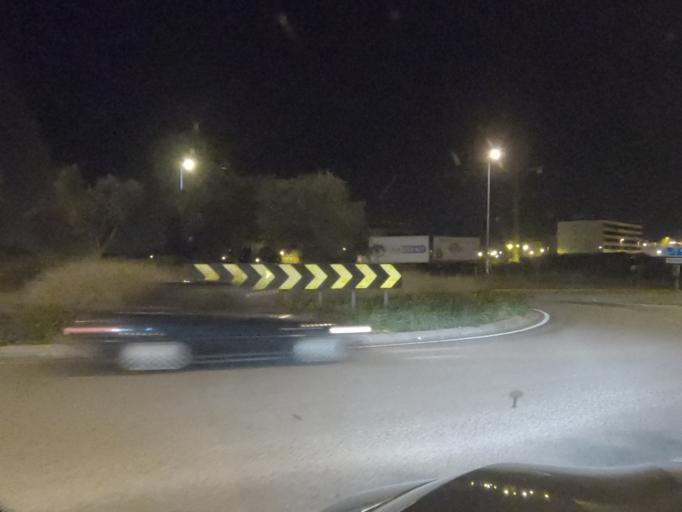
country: PT
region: Setubal
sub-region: Montijo
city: Montijo
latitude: 38.6976
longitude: -8.9445
